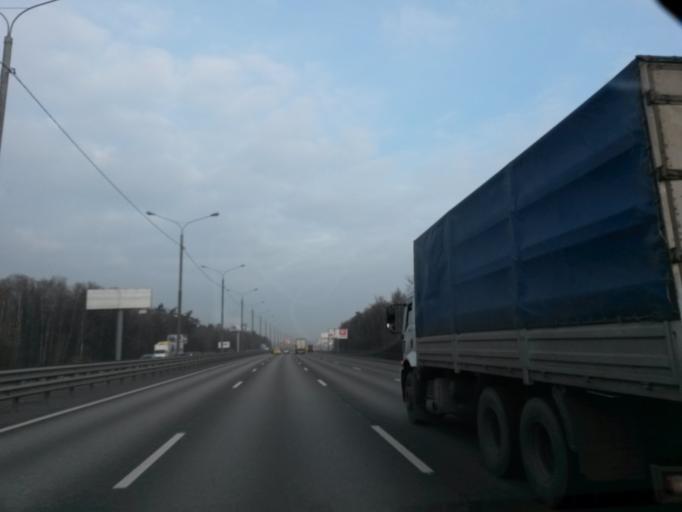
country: RU
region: Moskovskaya
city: Shcherbinka
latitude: 55.5140
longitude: 37.6087
